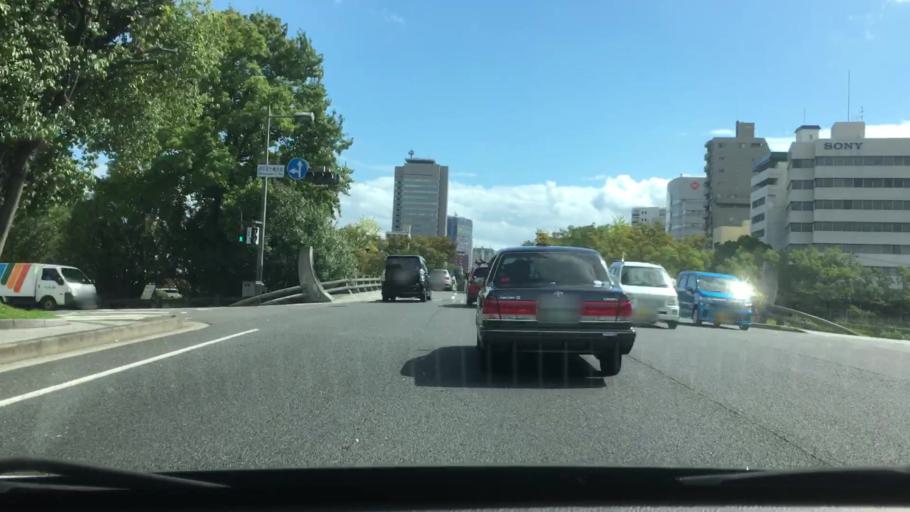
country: JP
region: Hiroshima
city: Hiroshima-shi
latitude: 34.3917
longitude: 132.4483
